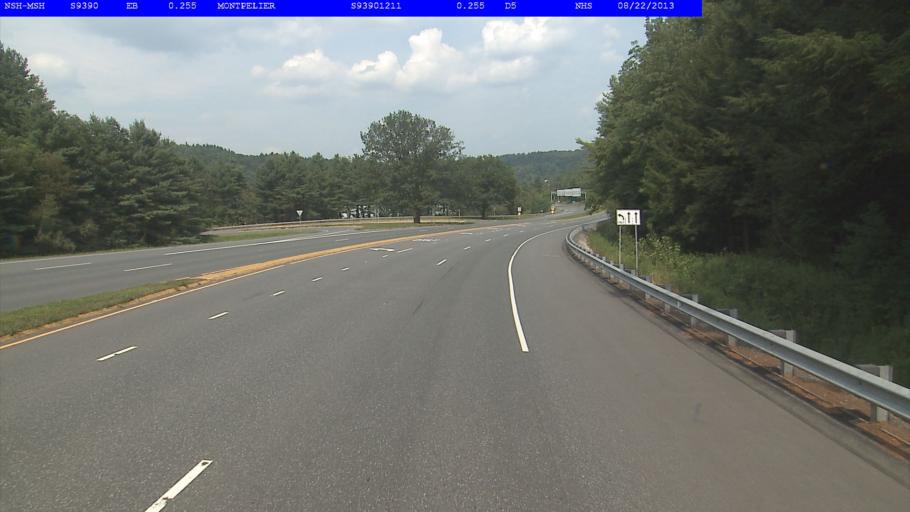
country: US
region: Vermont
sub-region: Washington County
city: Montpelier
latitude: 44.2538
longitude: -72.5938
